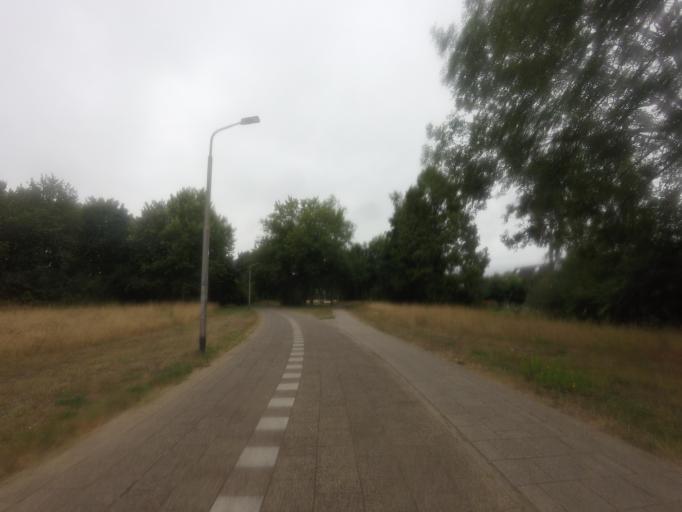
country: NL
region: Gelderland
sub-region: Gemeente Nijmegen
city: Lindenholt
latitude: 51.8356
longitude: 5.8069
